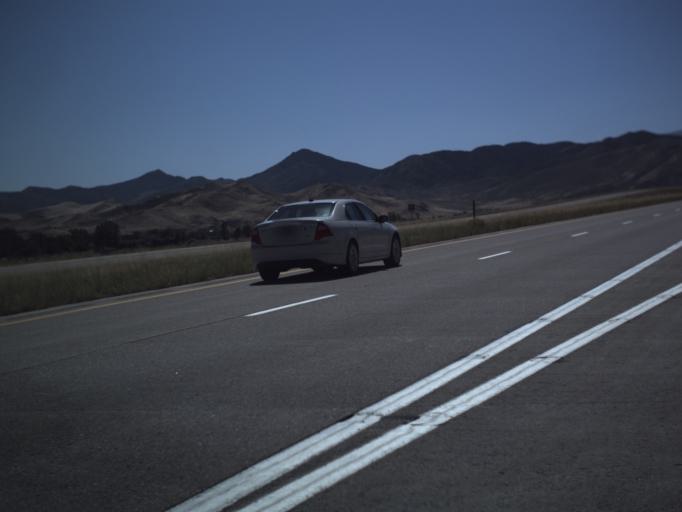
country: US
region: Utah
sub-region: Sevier County
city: Monroe
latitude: 38.6316
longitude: -112.2240
